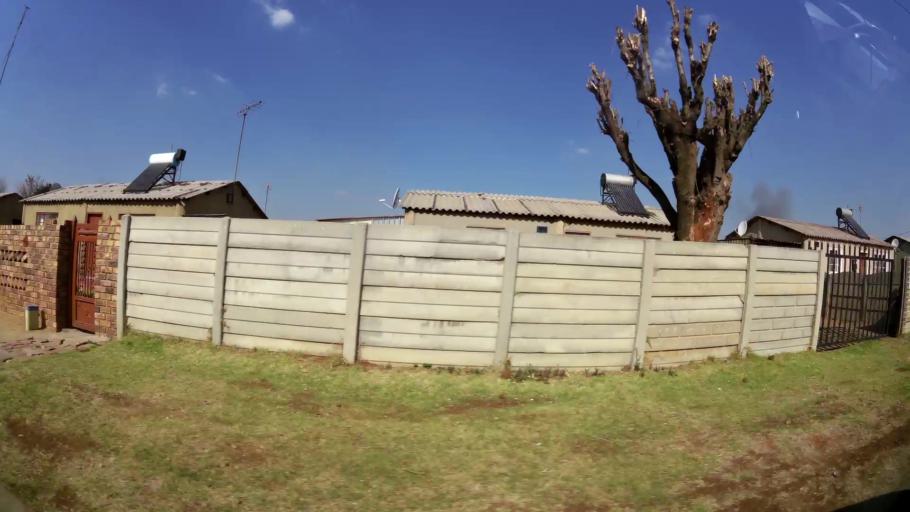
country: ZA
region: Gauteng
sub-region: Ekurhuleni Metropolitan Municipality
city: Benoni
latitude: -26.1436
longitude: 28.4094
